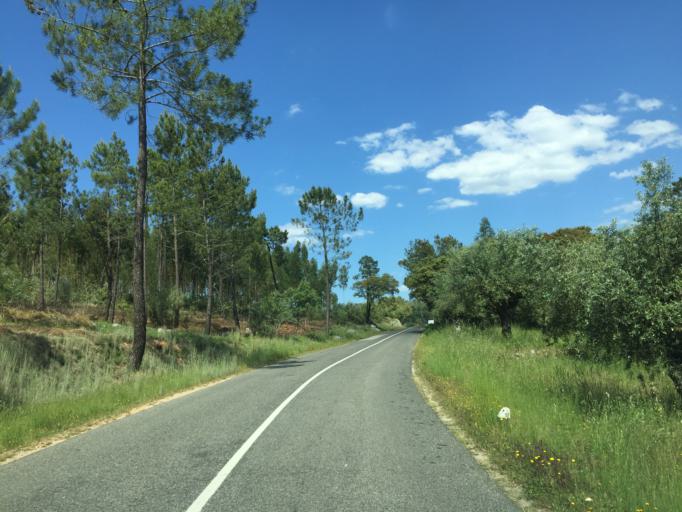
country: PT
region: Leiria
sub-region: Alvaiazere
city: Alvaiazere
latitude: 39.7834
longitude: -8.4401
